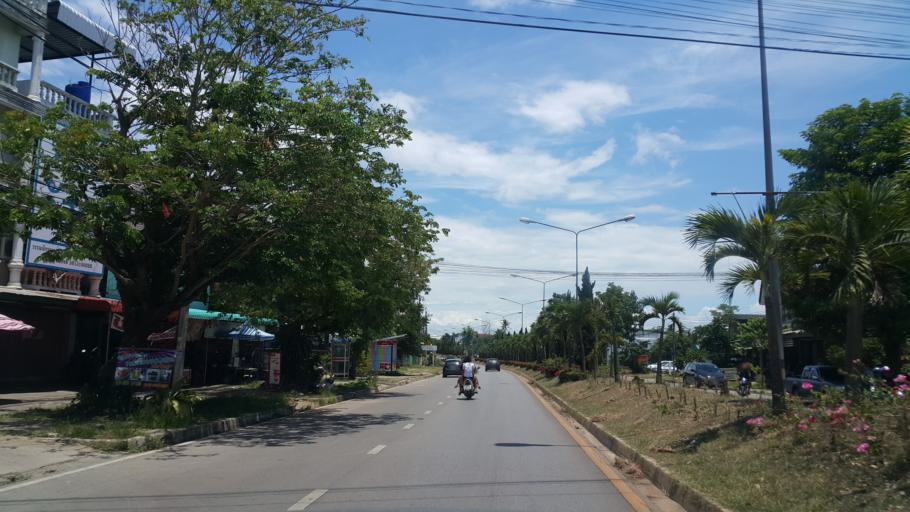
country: TH
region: Phayao
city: Phayao
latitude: 19.1872
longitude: 99.8793
